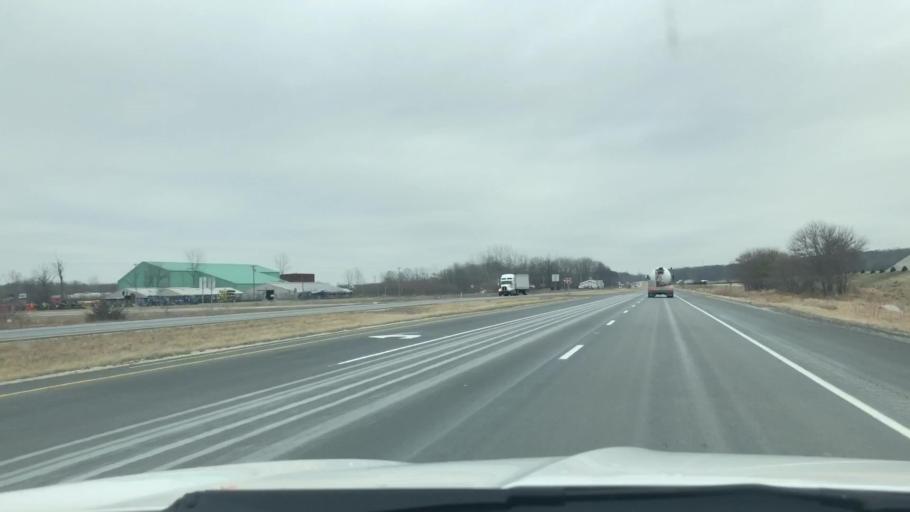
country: US
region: Indiana
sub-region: Cass County
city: Logansport
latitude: 40.7339
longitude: -86.3404
